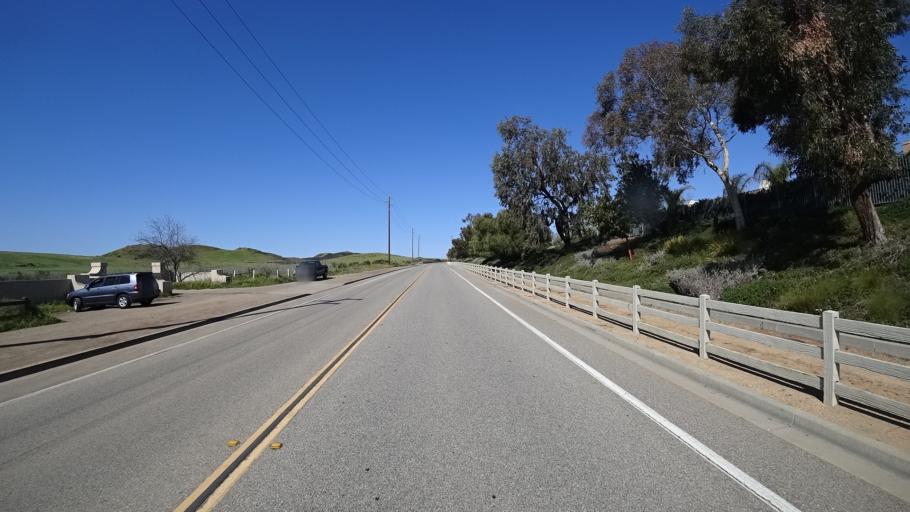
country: US
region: California
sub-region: Ventura County
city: Casa Conejo
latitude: 34.1564
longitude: -118.9858
